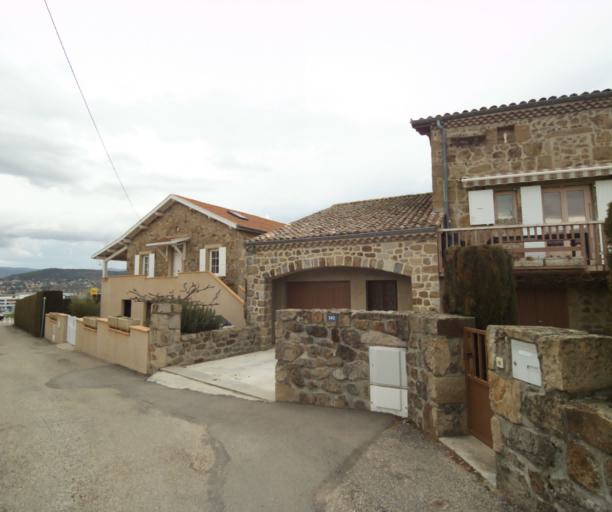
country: FR
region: Rhone-Alpes
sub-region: Departement de l'Ardeche
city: Davezieux
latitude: 45.2577
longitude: 4.6994
